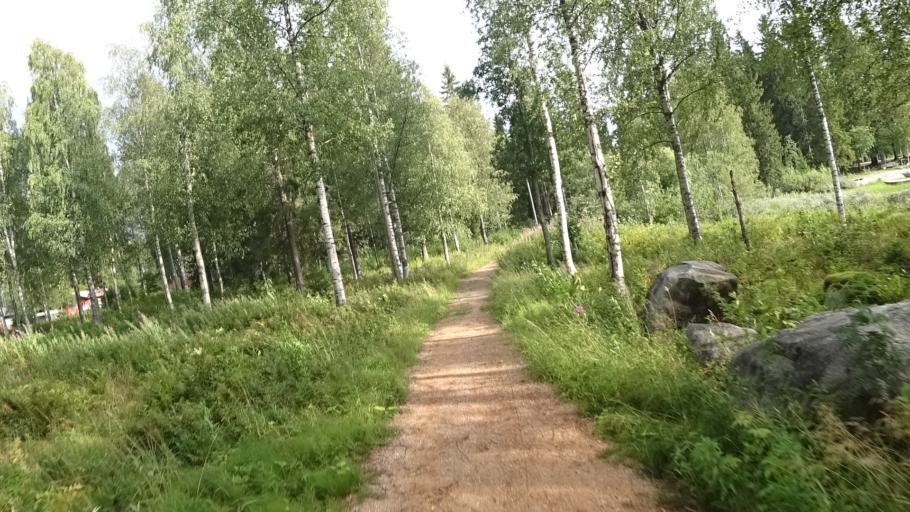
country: FI
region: North Karelia
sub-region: Joensuu
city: Ilomantsi
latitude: 62.6666
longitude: 30.9116
